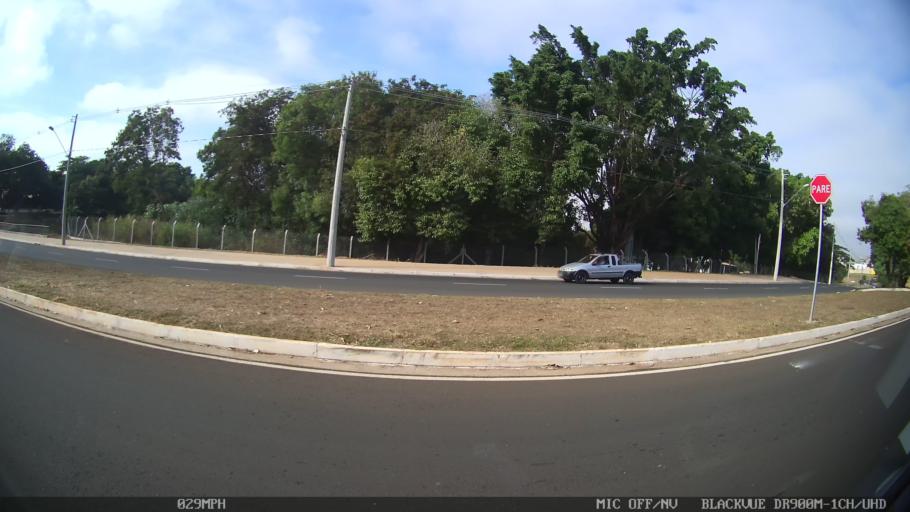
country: BR
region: Sao Paulo
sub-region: Sao Jose Do Rio Preto
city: Sao Jose do Rio Preto
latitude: -20.7951
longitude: -49.4260
